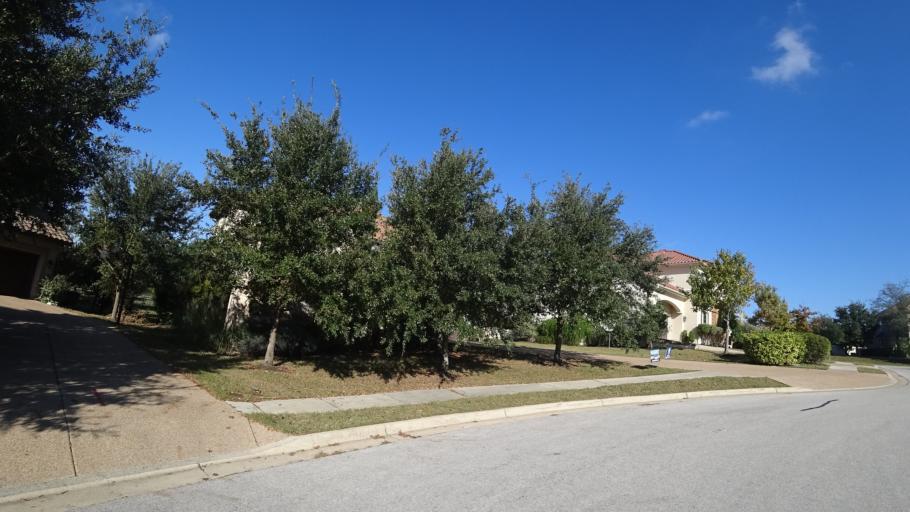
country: US
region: Texas
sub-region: Travis County
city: Bee Cave
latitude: 30.3498
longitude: -97.8958
